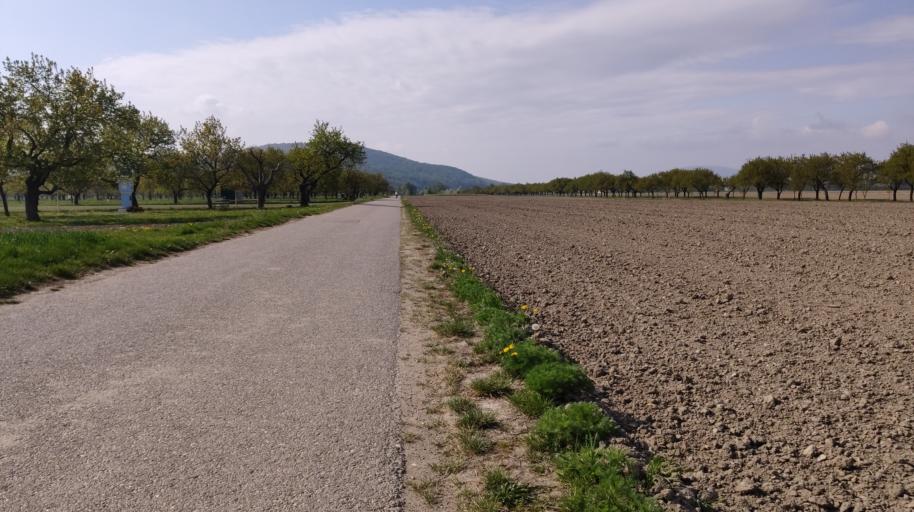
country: AT
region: Burgenland
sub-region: Politischer Bezirk Neusiedl am See
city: Kittsee
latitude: 48.1005
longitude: 17.0563
